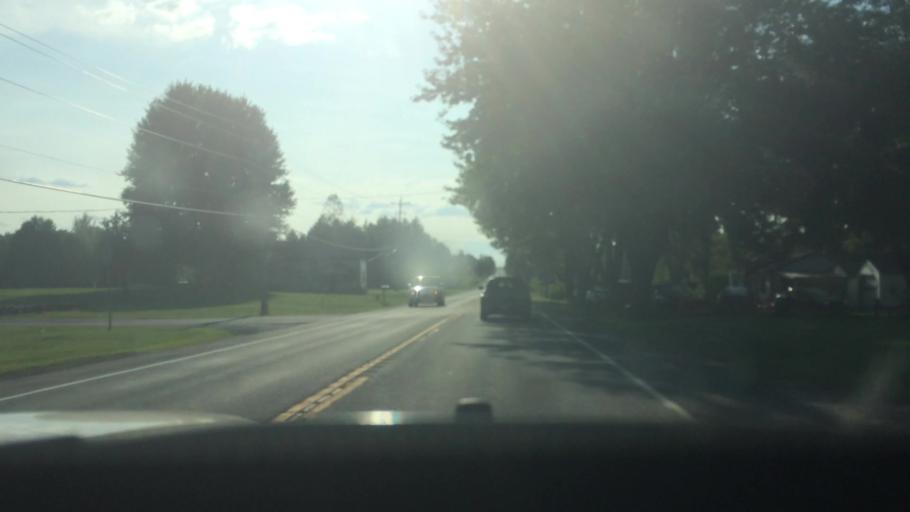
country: US
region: New York
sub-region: St. Lawrence County
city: Potsdam
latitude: 44.6702
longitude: -74.9205
